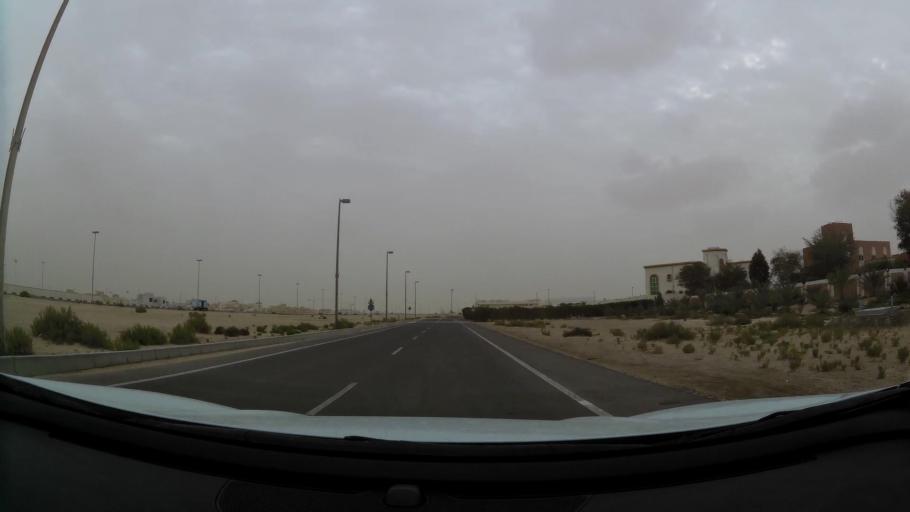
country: AE
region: Abu Dhabi
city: Abu Dhabi
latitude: 24.4267
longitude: 54.7253
